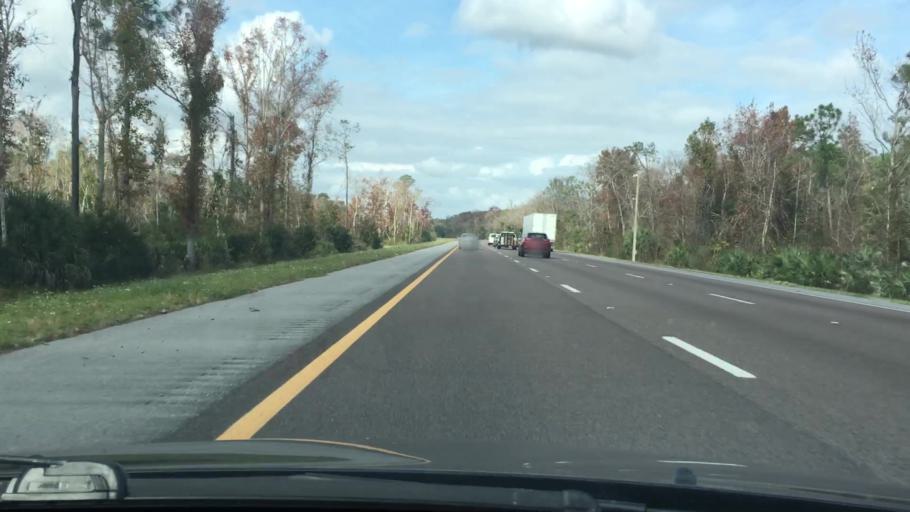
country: US
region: Florida
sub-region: Volusia County
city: Edgewater
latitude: 28.9213
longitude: -80.9374
